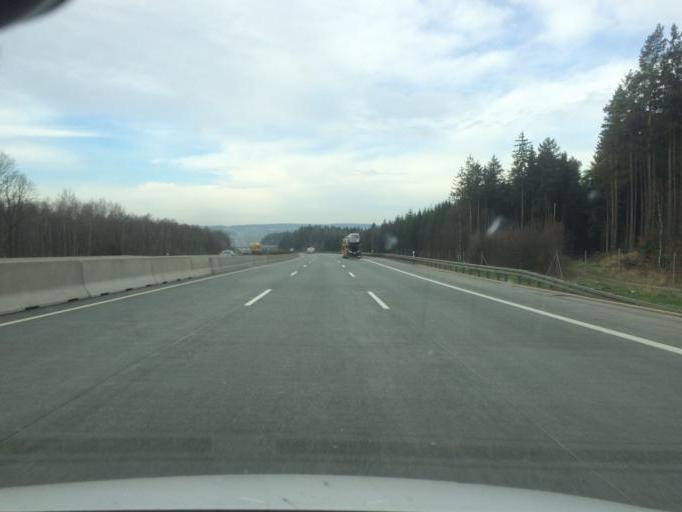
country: DE
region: Thuringia
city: Lemnitz
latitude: 50.7024
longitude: 11.8457
